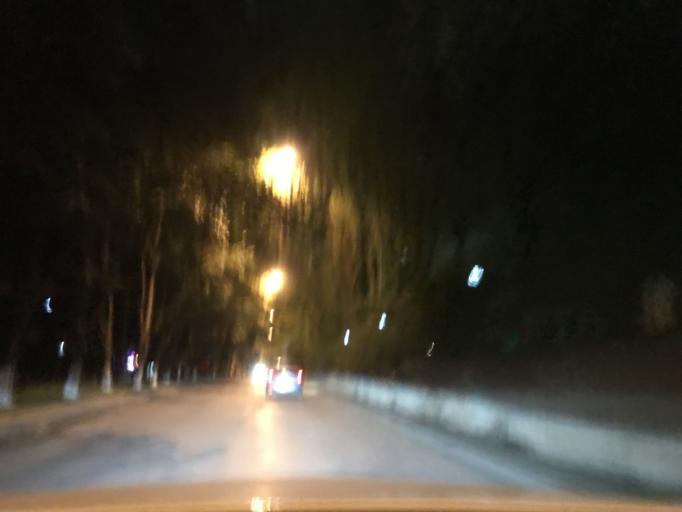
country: CN
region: Sichuan
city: Mianyang
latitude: 31.4520
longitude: 104.7590
